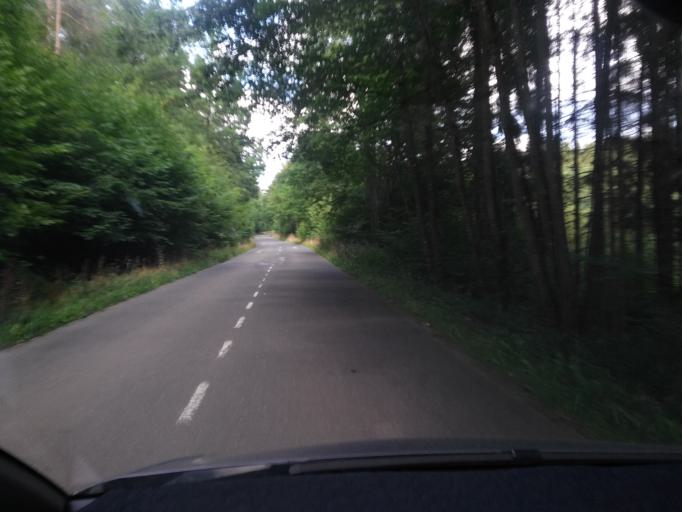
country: BE
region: Wallonia
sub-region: Province du Luxembourg
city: Libin
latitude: 50.0238
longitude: 5.3033
